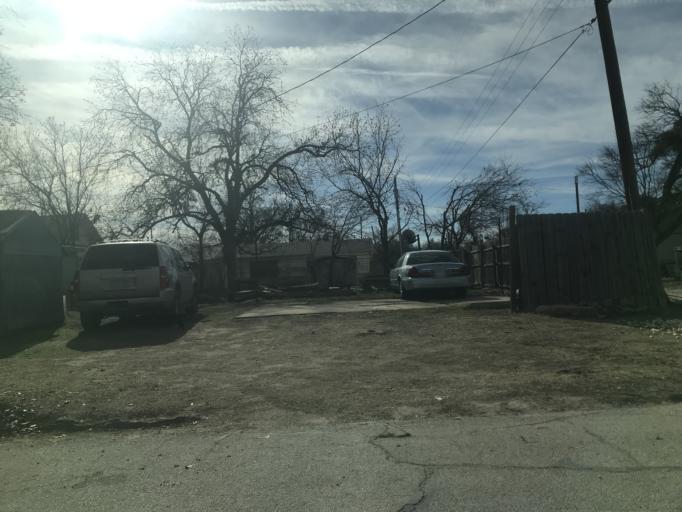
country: US
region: Texas
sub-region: Taylor County
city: Abilene
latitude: 32.4440
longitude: -99.7429
